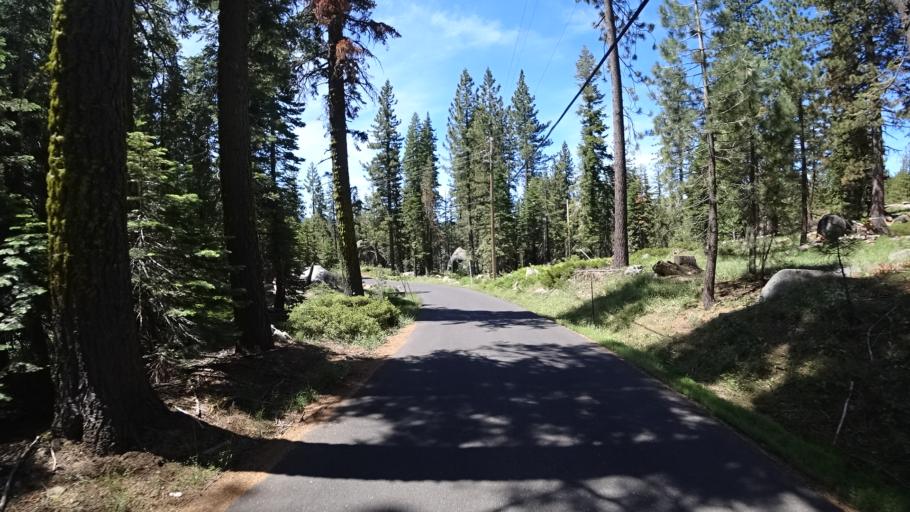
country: US
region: California
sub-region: Calaveras County
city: Arnold
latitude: 38.4213
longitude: -120.0971
